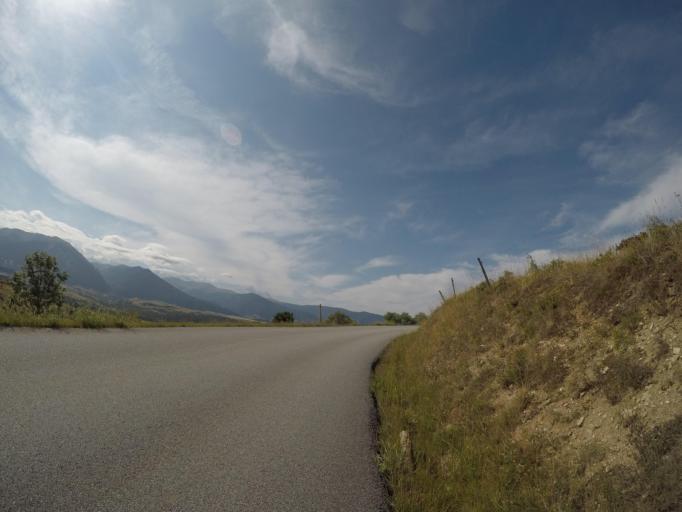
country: ES
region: Catalonia
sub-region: Provincia de Girona
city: Llivia
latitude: 42.4984
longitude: 2.0559
